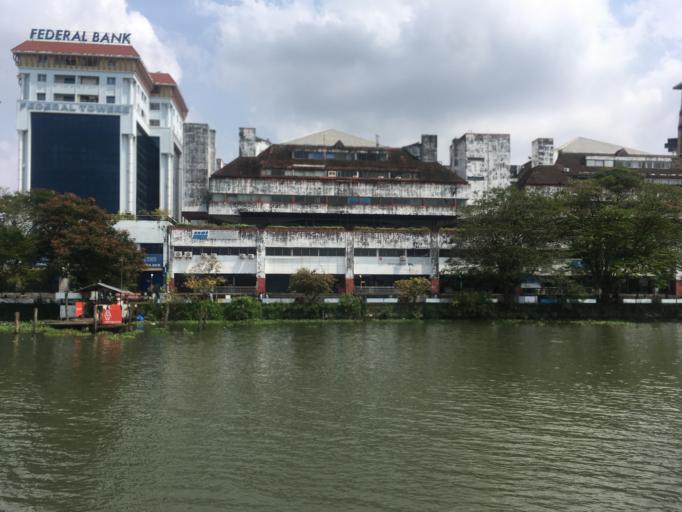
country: IN
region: Kerala
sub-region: Ernakulam
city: Cochin
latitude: 9.9782
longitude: 76.2752
